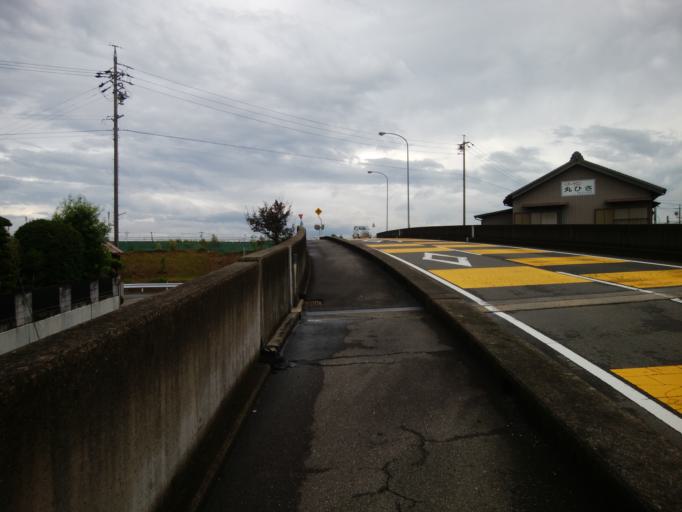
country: JP
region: Aichi
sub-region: Aisai-shi
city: Aisai
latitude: 35.1550
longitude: 136.7591
